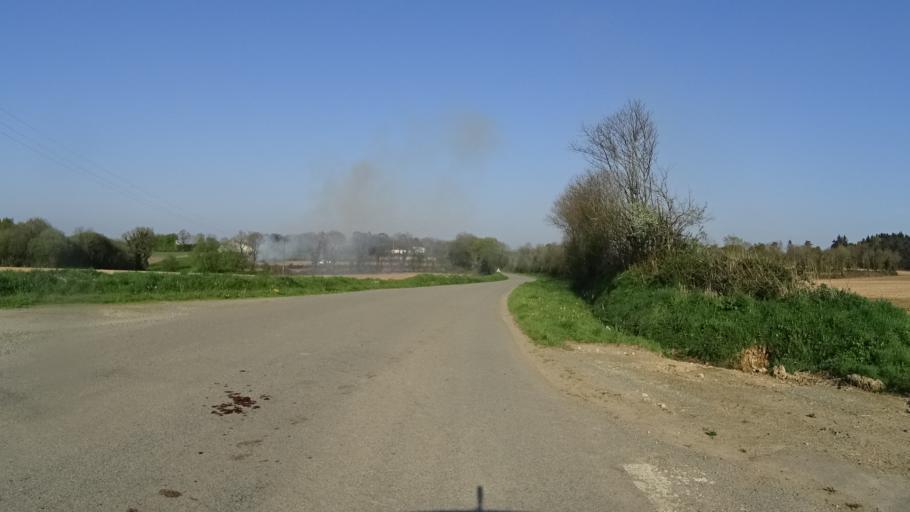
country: FR
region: Brittany
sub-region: Departement du Finistere
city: Sizun
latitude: 48.3975
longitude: -4.1116
